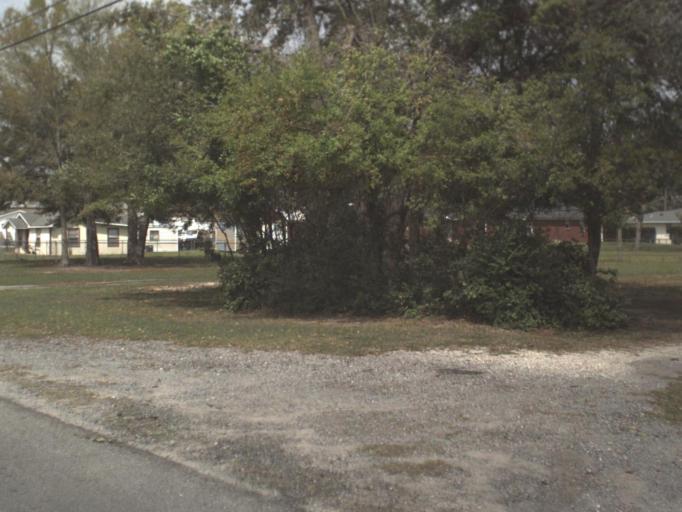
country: US
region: Florida
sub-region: Escambia County
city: Myrtle Grove
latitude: 30.3734
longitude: -87.3250
